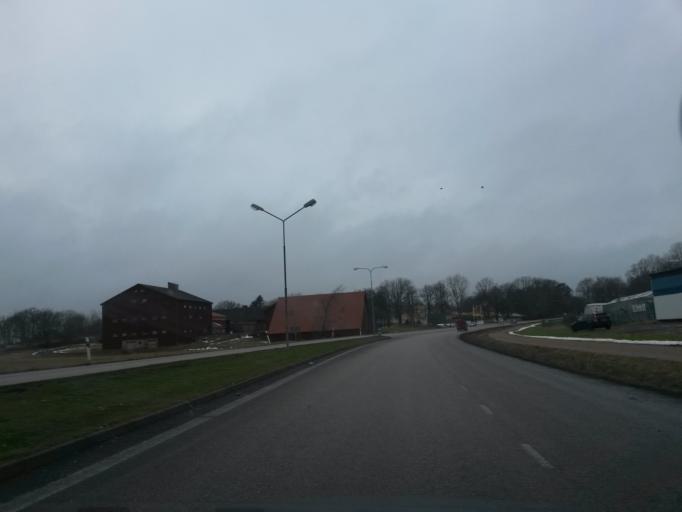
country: SE
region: Vaestra Goetaland
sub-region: Vanersborgs Kommun
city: Vargon
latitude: 58.3526
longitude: 12.3918
